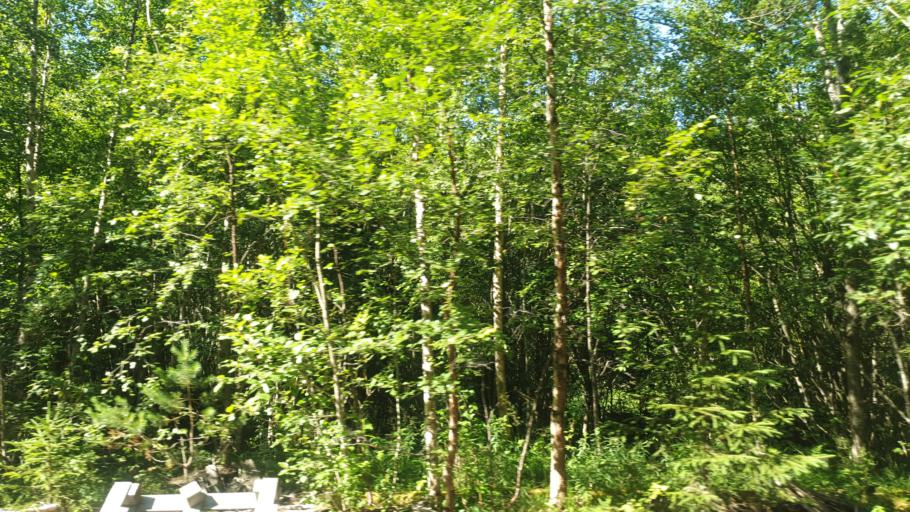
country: NO
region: Sor-Trondelag
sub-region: Meldal
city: Meldal
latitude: 63.1373
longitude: 9.7110
